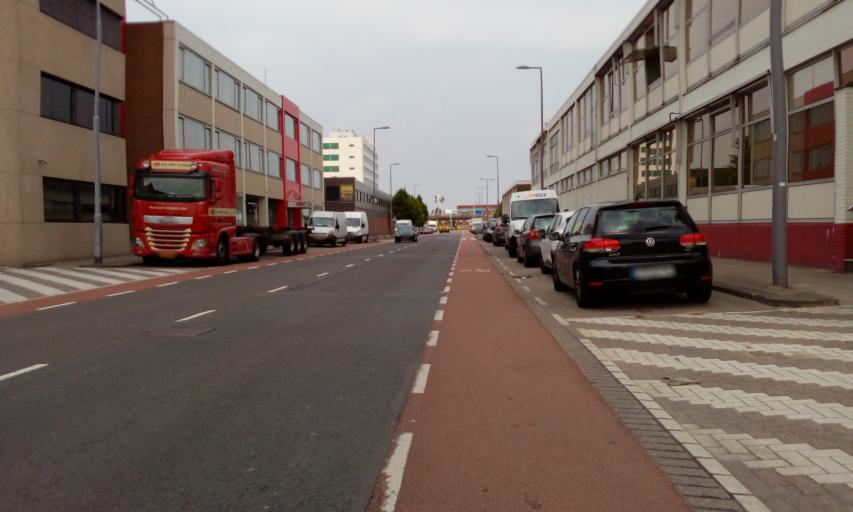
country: NL
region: South Holland
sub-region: Gemeente Rotterdam
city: Delfshaven
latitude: 51.9232
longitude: 4.4267
